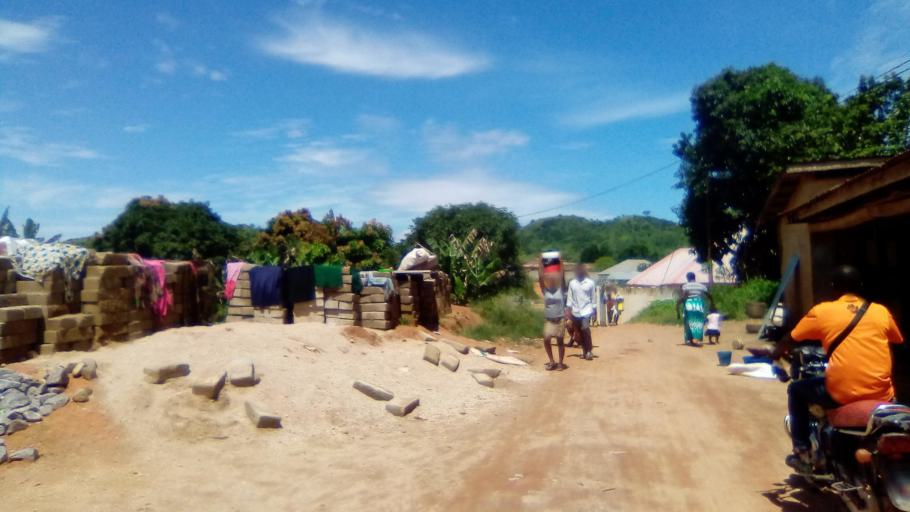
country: SL
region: Eastern Province
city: Simbakoro
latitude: 8.6223
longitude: -10.9957
